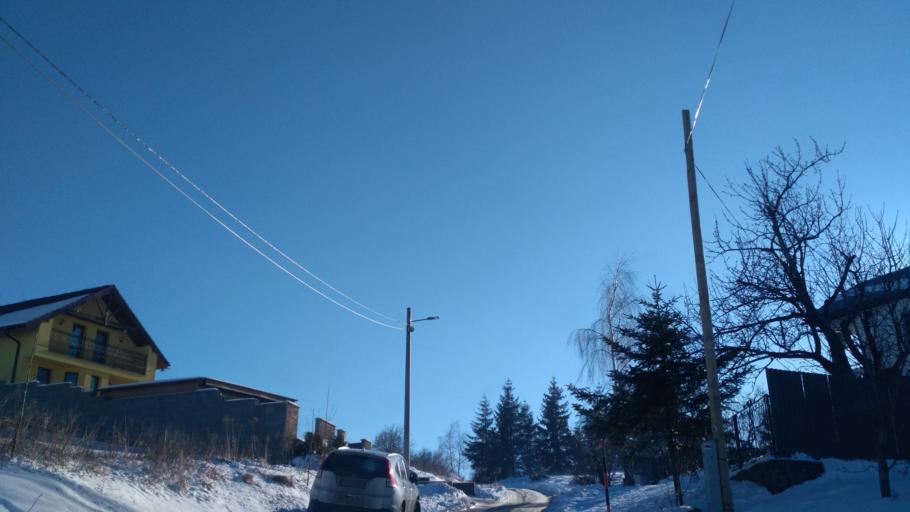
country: SK
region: Kosicky
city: Kosice
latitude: 48.7708
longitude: 21.2056
